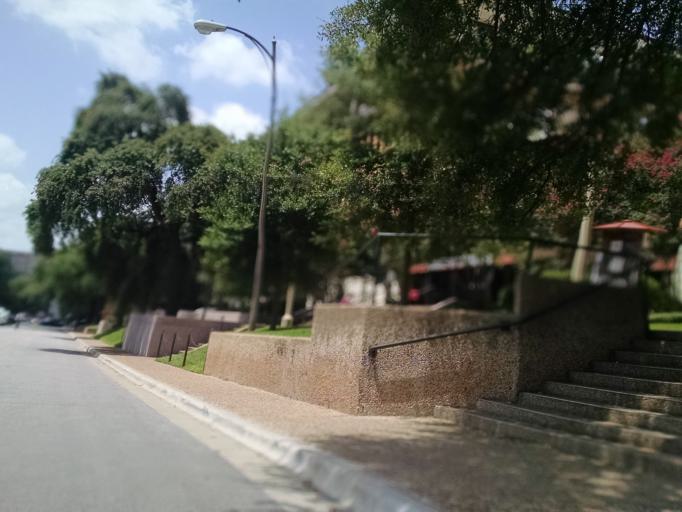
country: US
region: Texas
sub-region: Travis County
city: Austin
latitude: 30.2847
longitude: -97.7374
